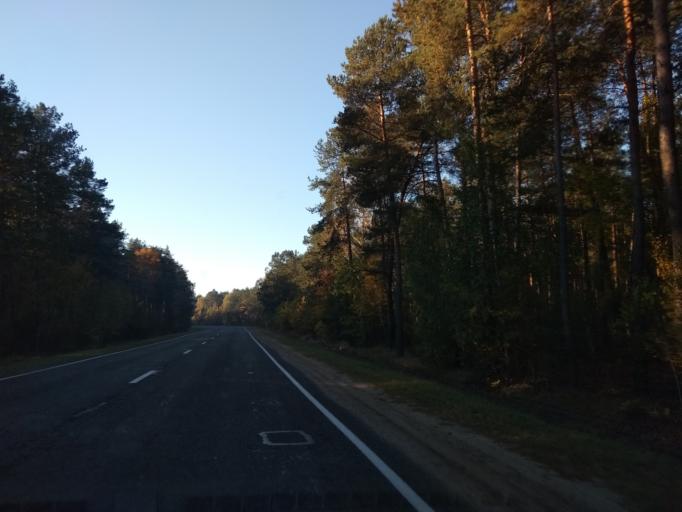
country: BY
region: Brest
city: Kobryn
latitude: 52.1004
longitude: 24.2789
